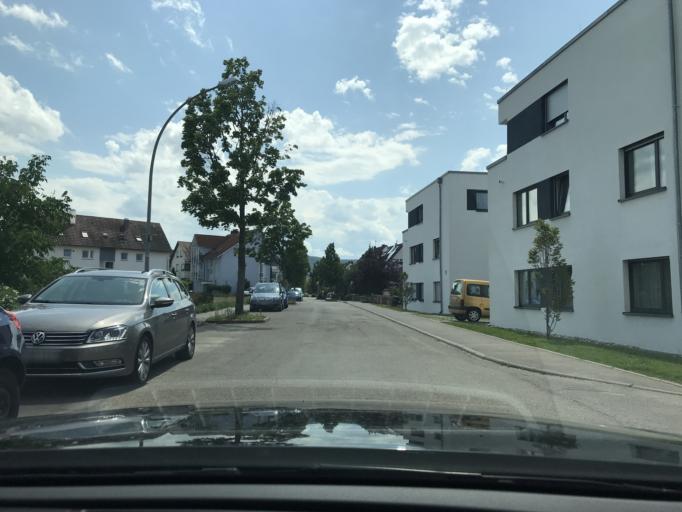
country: DE
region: Baden-Wuerttemberg
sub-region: Regierungsbezirk Stuttgart
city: Waiblingen
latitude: 48.8111
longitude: 9.3273
